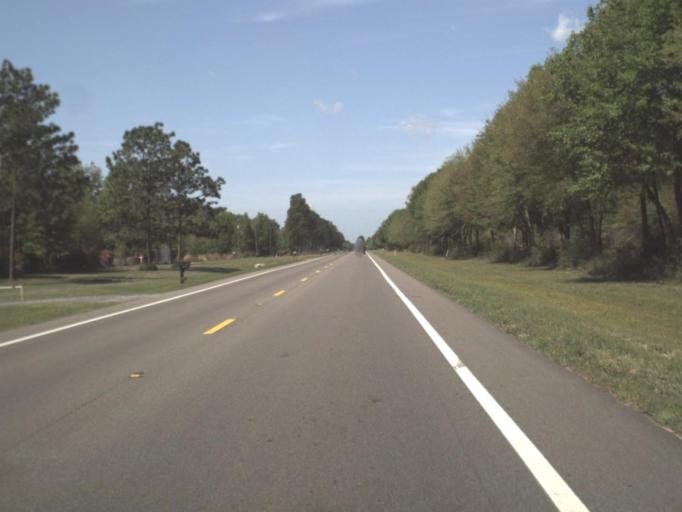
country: US
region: Florida
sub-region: Santa Rosa County
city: East Milton
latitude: 30.6464
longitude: -86.9220
